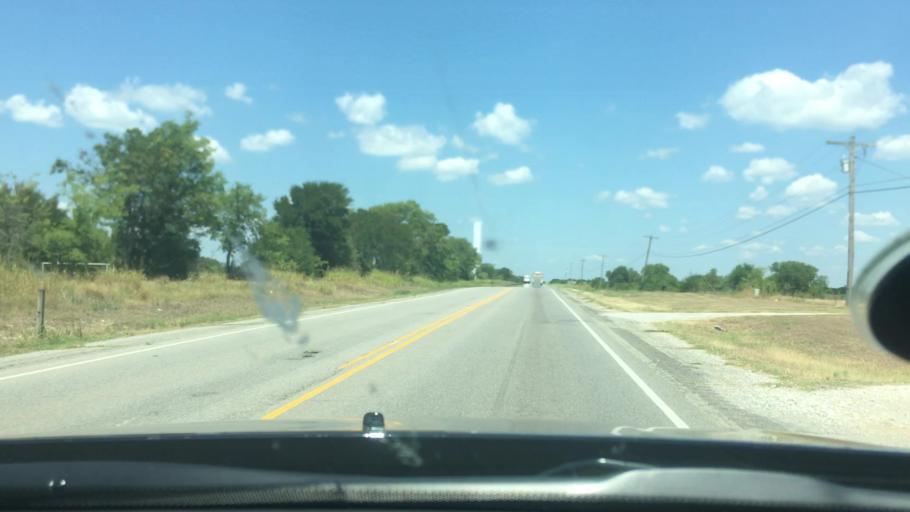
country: US
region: Oklahoma
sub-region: Marshall County
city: Oakland
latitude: 34.1359
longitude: -96.7971
